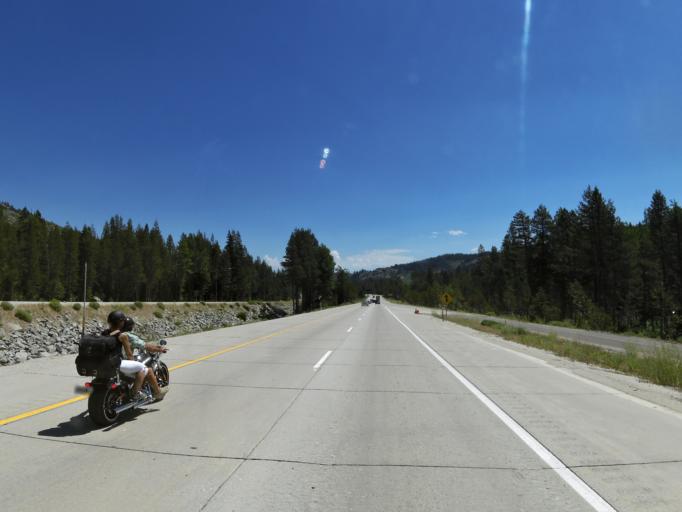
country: US
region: California
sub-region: Nevada County
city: Truckee
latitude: 39.3117
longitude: -120.4985
